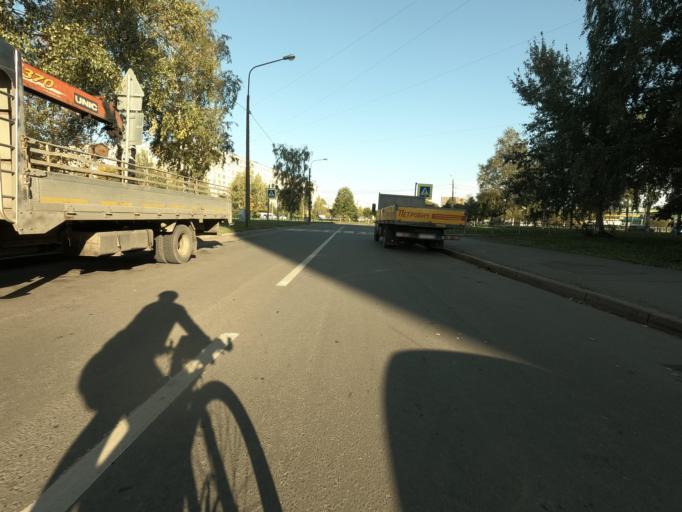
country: RU
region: St.-Petersburg
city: Kolpino
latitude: 59.7381
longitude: 30.5676
